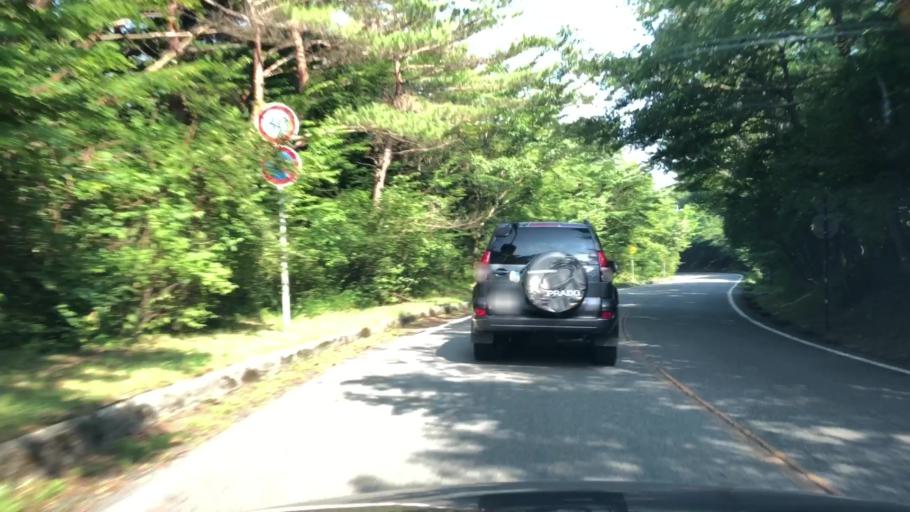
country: JP
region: Shizuoka
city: Gotemba
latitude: 35.3336
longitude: 138.8182
